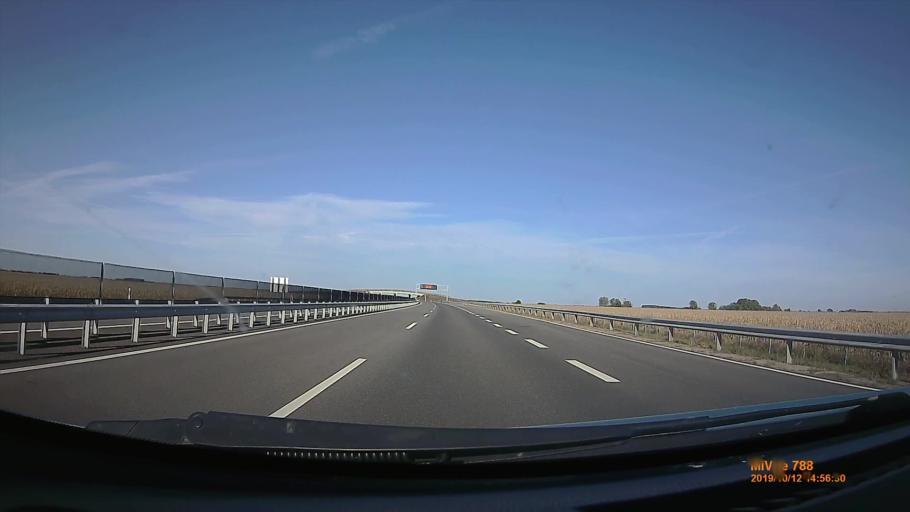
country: HU
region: Hajdu-Bihar
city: Derecske
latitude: 47.4195
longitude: 21.5609
